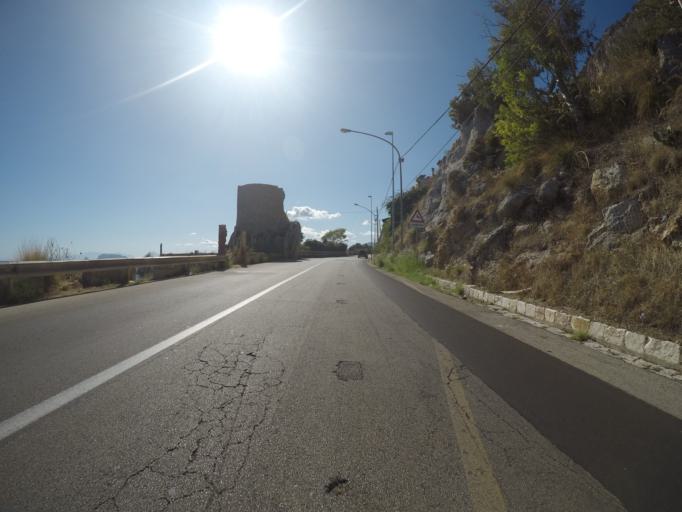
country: IT
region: Sicily
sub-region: Palermo
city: Palermo
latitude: 38.1794
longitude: 13.3660
